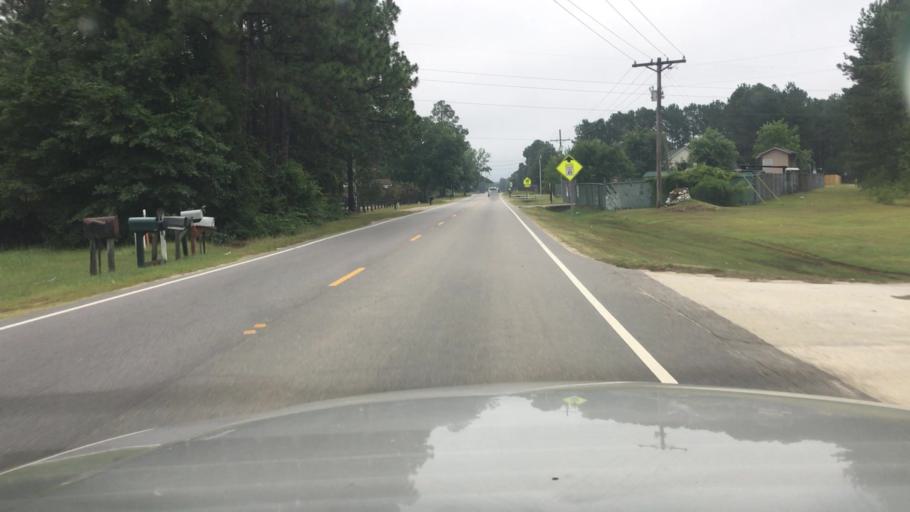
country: US
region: North Carolina
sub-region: Hoke County
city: Rockfish
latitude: 34.9712
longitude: -79.0163
